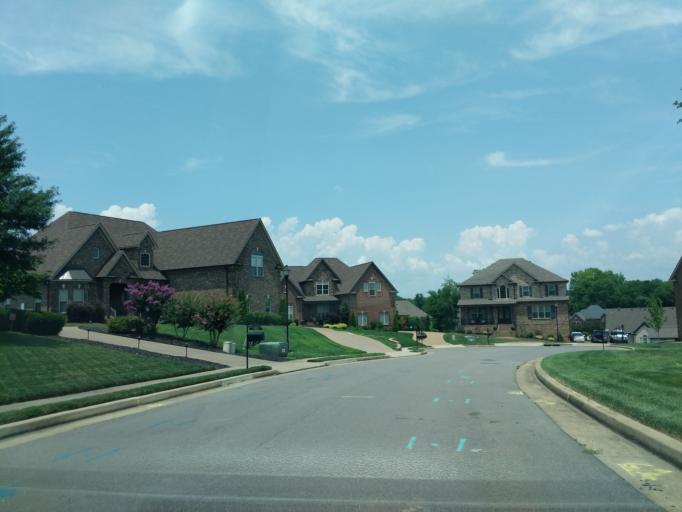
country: US
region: Tennessee
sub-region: Davidson County
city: Lakewood
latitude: 36.2317
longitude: -86.6330
